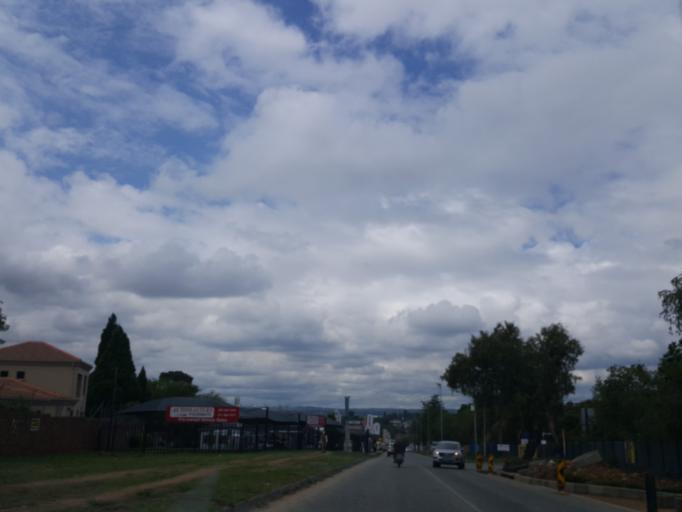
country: ZA
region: Gauteng
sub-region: City of Johannesburg Metropolitan Municipality
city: Diepsloot
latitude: -26.0101
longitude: 28.0009
